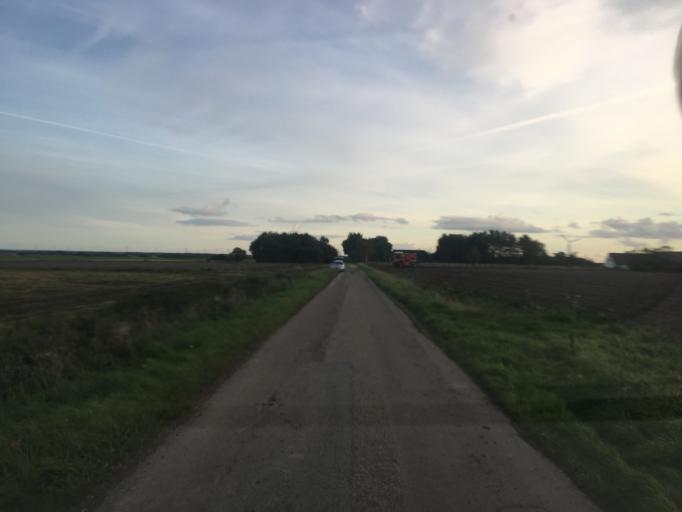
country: DK
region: South Denmark
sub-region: Tonder Kommune
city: Tonder
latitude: 54.9739
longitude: 8.9043
